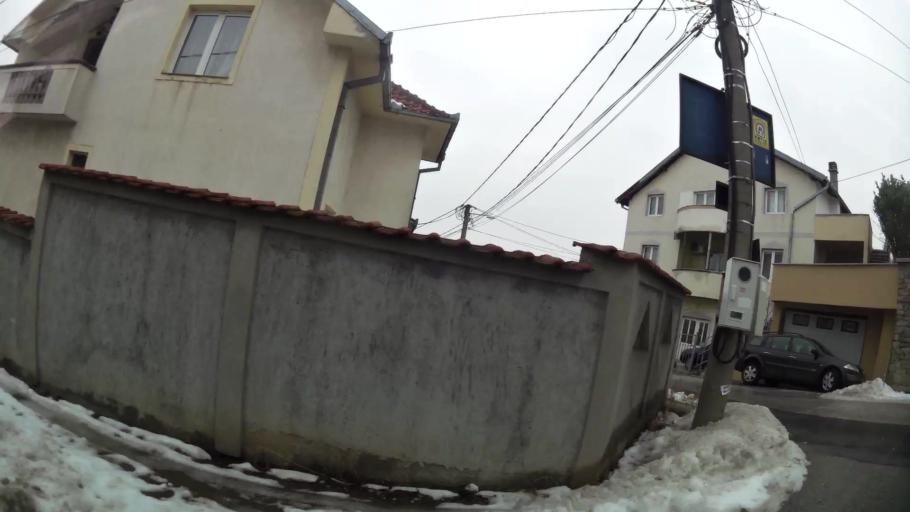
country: RS
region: Central Serbia
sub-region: Belgrade
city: Zvezdara
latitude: 44.7678
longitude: 20.5079
